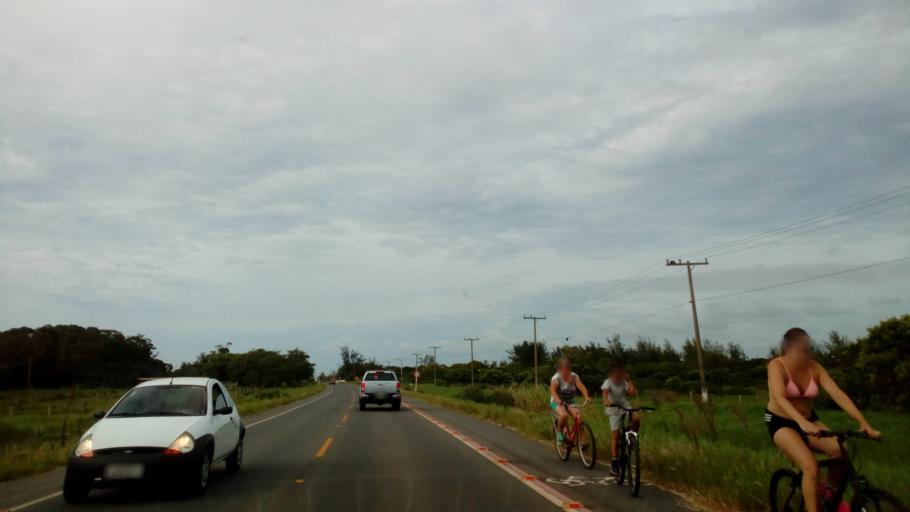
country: BR
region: Santa Catarina
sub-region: Laguna
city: Laguna
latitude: -28.5532
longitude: -48.7998
